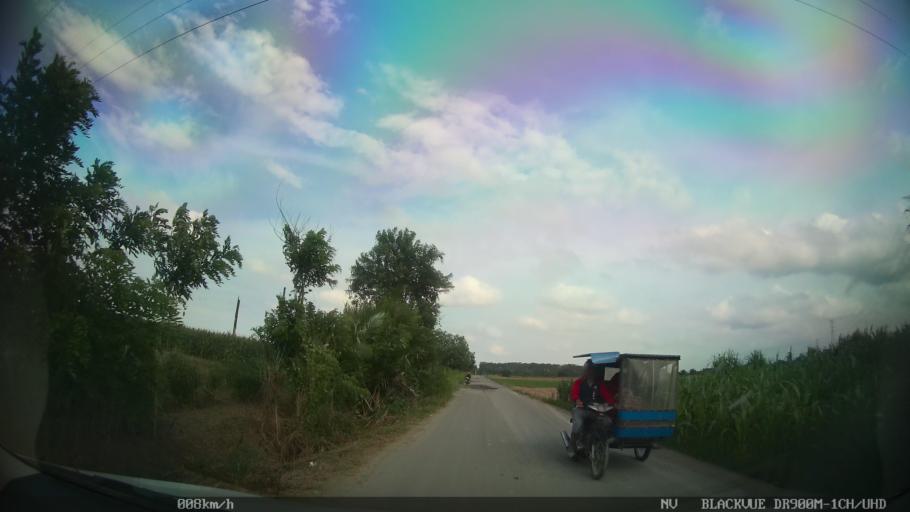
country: ID
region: North Sumatra
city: Percut
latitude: 3.5678
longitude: 98.7834
